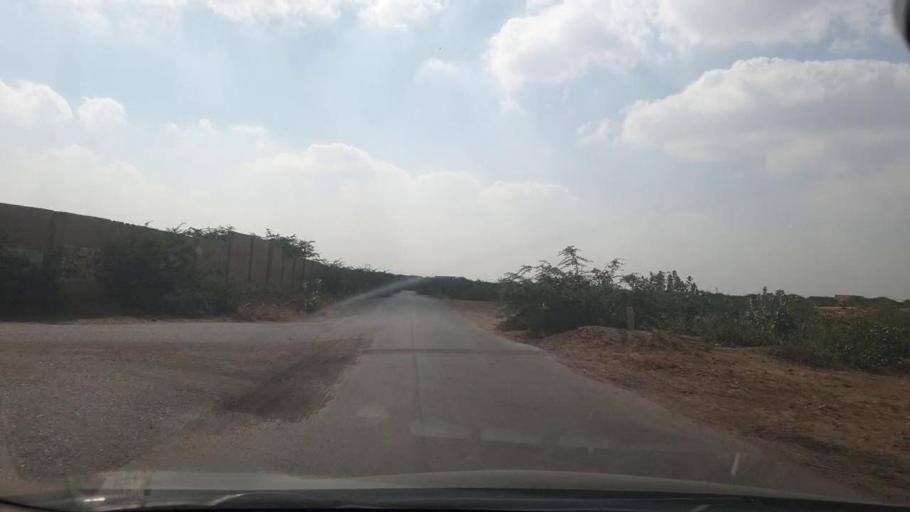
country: PK
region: Sindh
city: Malir Cantonment
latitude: 25.0168
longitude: 67.3533
